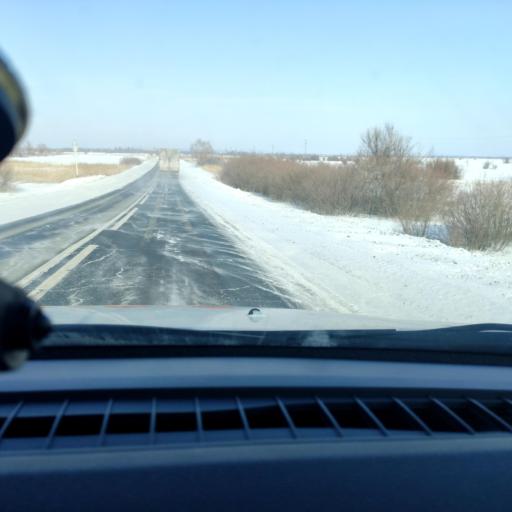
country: RU
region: Samara
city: Smyshlyayevka
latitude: 53.1568
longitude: 50.4568
